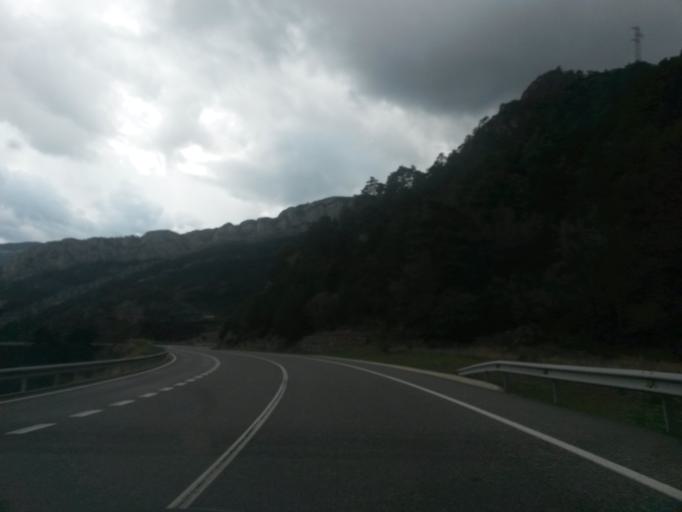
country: ES
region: Catalonia
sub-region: Provincia de Barcelona
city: Baga
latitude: 42.2890
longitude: 1.8540
